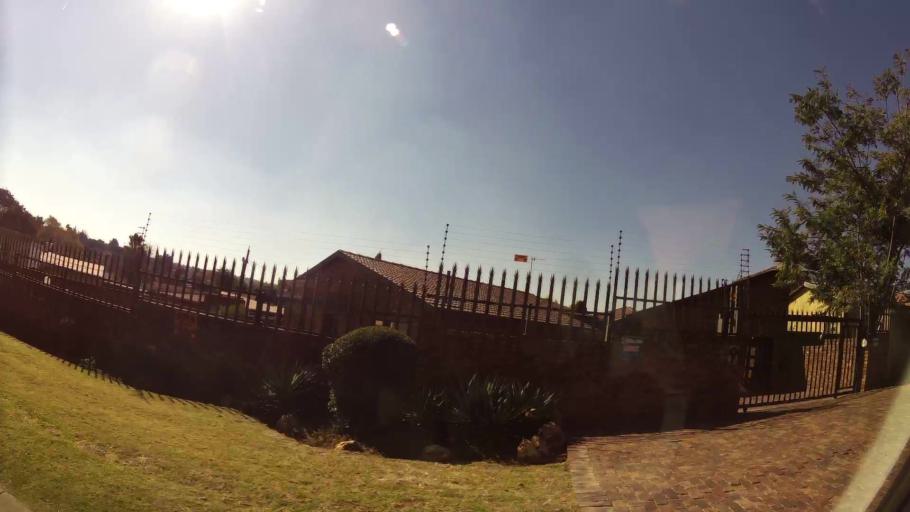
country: ZA
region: Gauteng
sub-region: City of Johannesburg Metropolitan Municipality
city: Johannesburg
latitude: -26.2790
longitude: 27.9944
